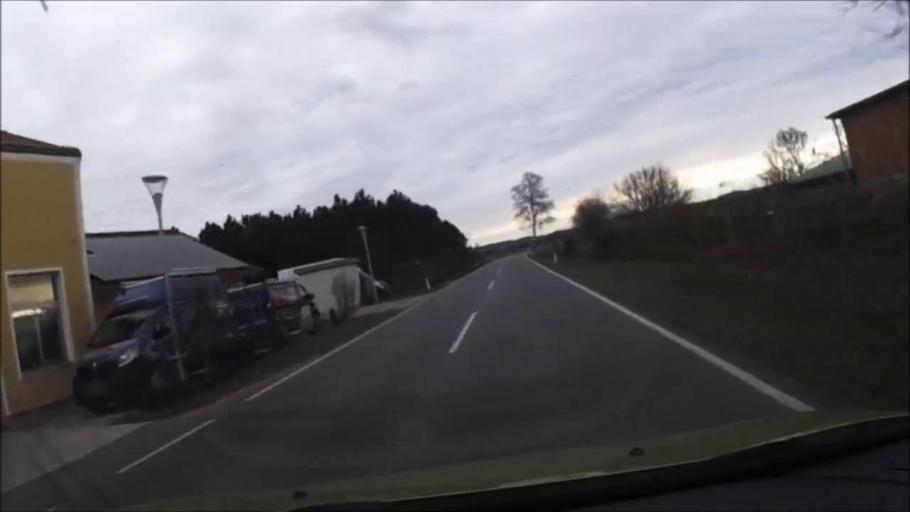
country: AT
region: Burgenland
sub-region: Eisenstadt-Umgebung
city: Leithaprodersdorf
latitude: 47.9501
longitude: 16.4520
